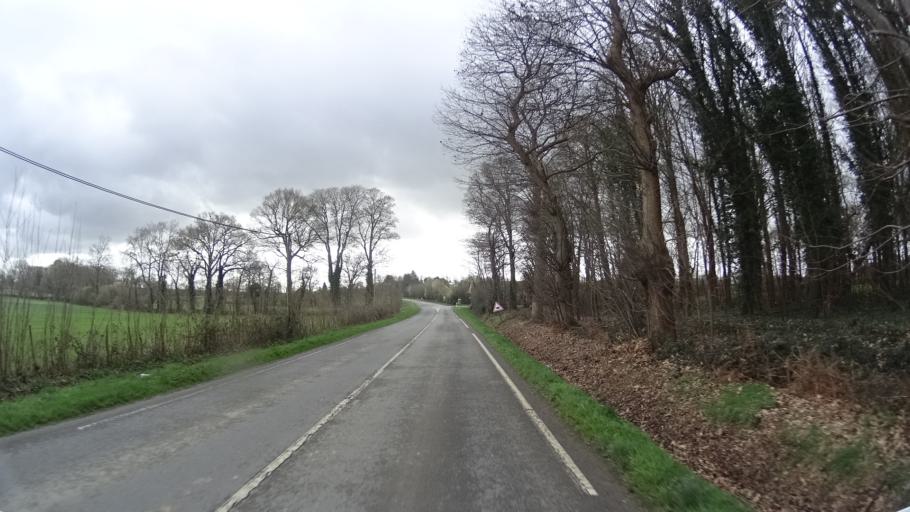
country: FR
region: Brittany
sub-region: Departement d'Ille-et-Vilaine
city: Saint-Gilles
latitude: 48.1756
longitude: -1.8469
